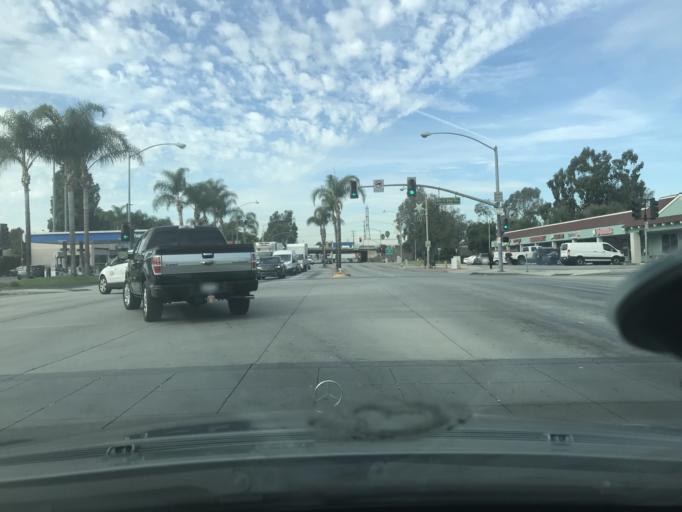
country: US
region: California
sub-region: Los Angeles County
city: Santa Fe Springs
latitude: 33.9487
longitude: -118.0893
